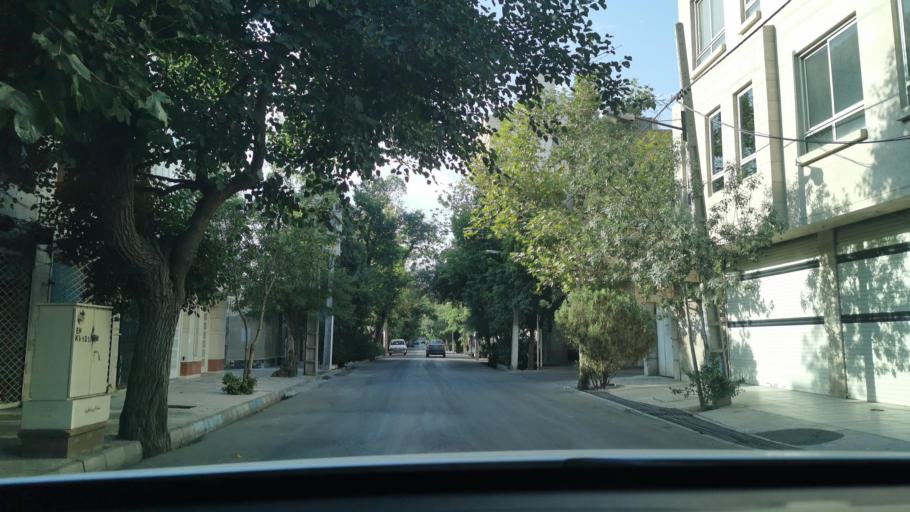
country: IR
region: Razavi Khorasan
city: Mashhad
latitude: 36.2956
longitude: 59.5835
